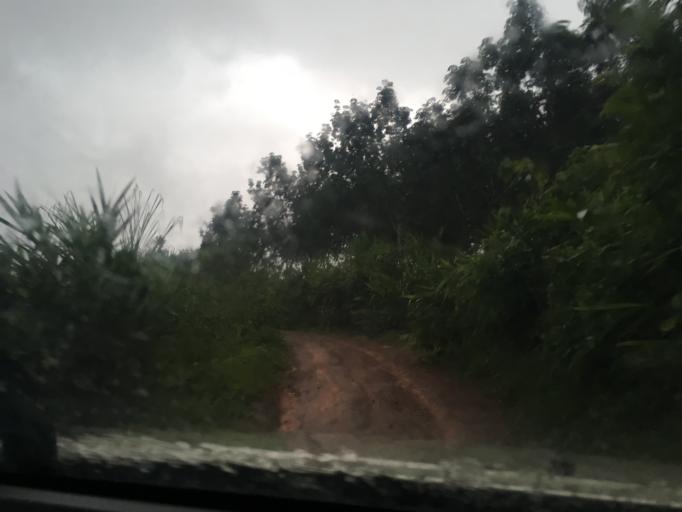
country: LA
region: Oudomxai
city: Muang La
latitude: 21.2424
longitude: 101.9438
